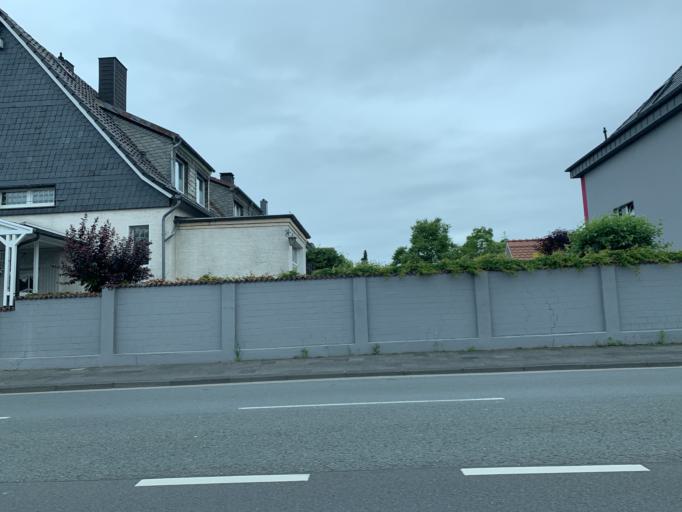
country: DE
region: North Rhine-Westphalia
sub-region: Regierungsbezirk Arnsberg
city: Hamm
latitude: 51.6677
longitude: 7.8264
